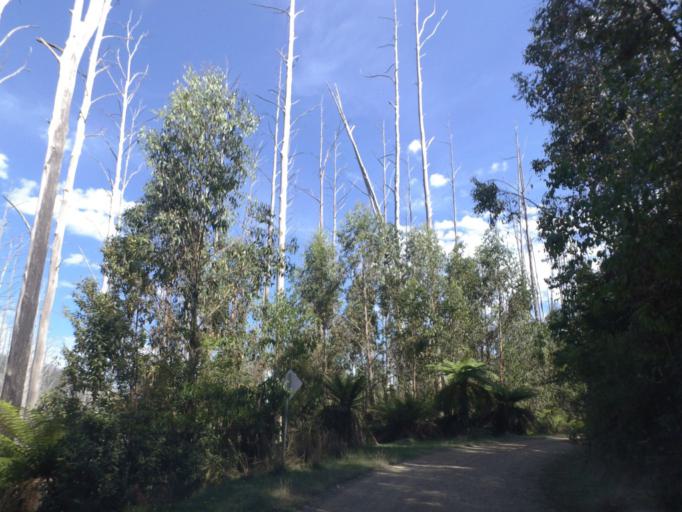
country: AU
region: Victoria
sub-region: Yarra Ranges
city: Millgrove
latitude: -37.4995
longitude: 145.8485
